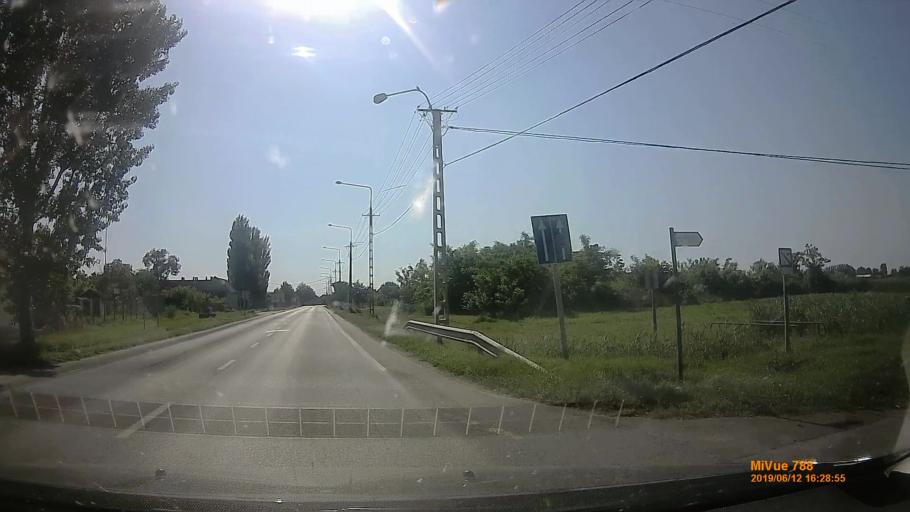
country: HU
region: Csongrad
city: Apatfalva
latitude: 46.1697
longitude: 20.6021
